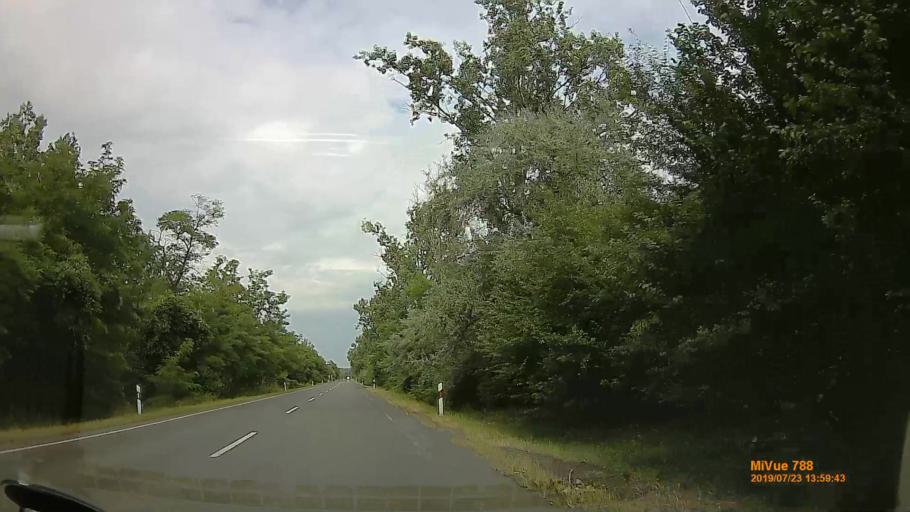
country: HU
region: Szabolcs-Szatmar-Bereg
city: Tiszavasvari
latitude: 47.9291
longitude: 21.2973
